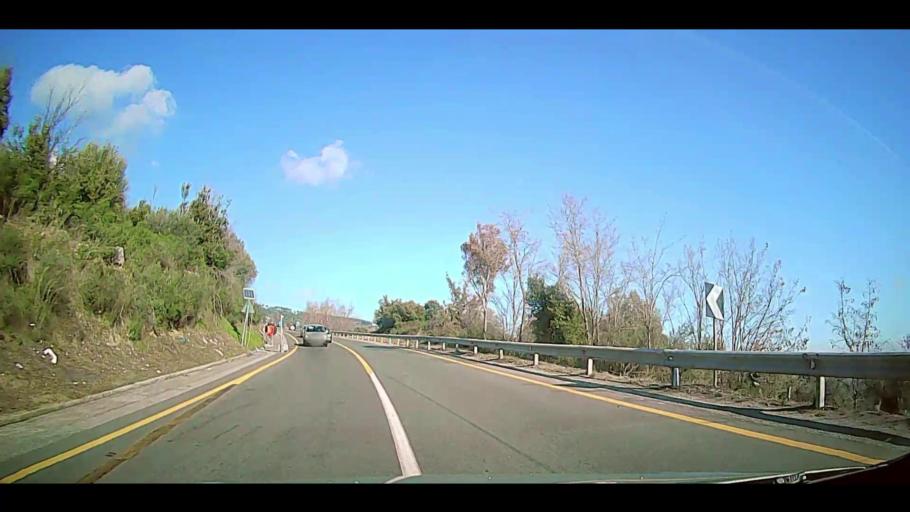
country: IT
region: Calabria
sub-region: Provincia di Crotone
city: Caccuri
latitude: 39.2262
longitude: 16.7958
